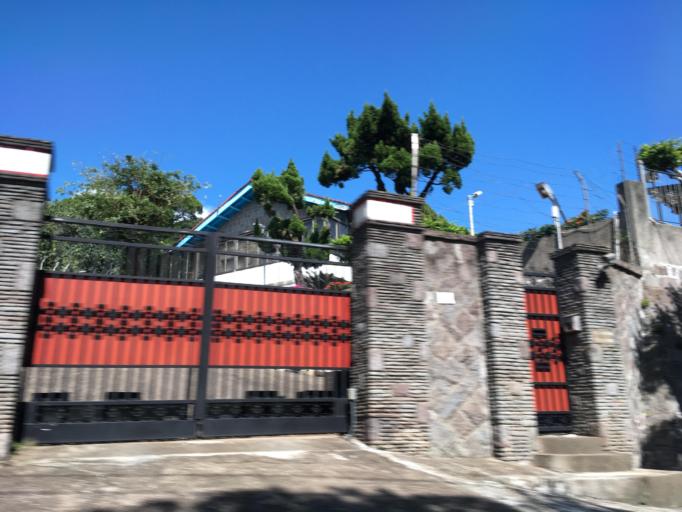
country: TW
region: Taipei
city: Taipei
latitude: 25.1505
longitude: 121.5043
